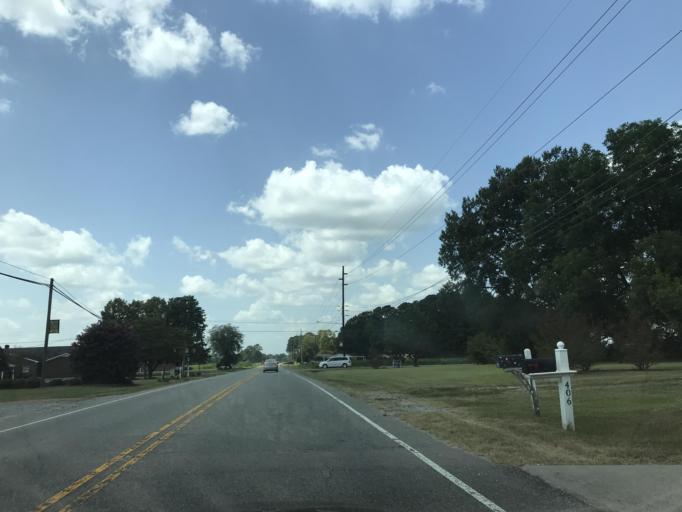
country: US
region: North Carolina
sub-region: Sampson County
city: Plain View
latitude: 35.2463
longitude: -78.3579
